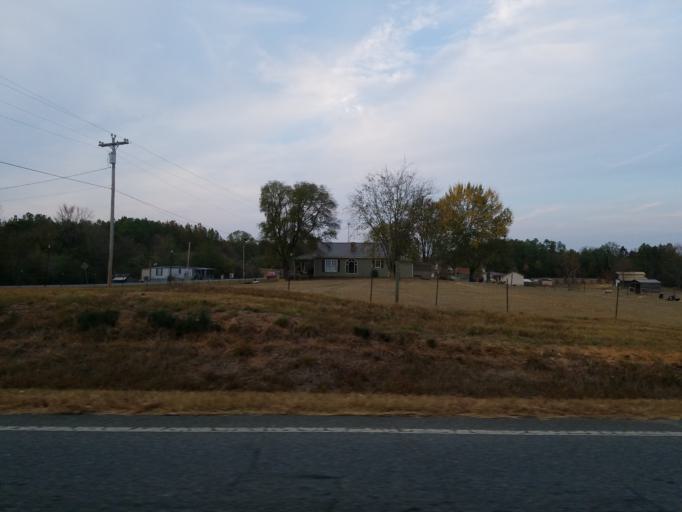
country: US
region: Georgia
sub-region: Gordon County
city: Calhoun
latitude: 34.6043
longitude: -84.8204
